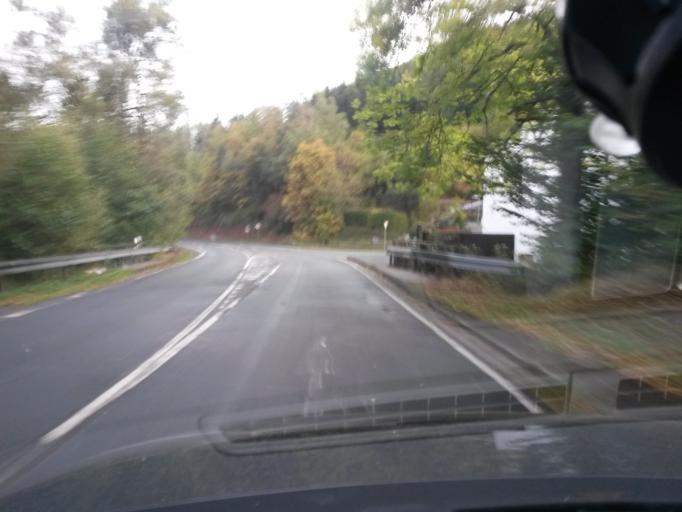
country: DE
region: North Rhine-Westphalia
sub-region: Regierungsbezirk Arnsberg
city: Herscheid
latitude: 51.2043
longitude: 7.7221
